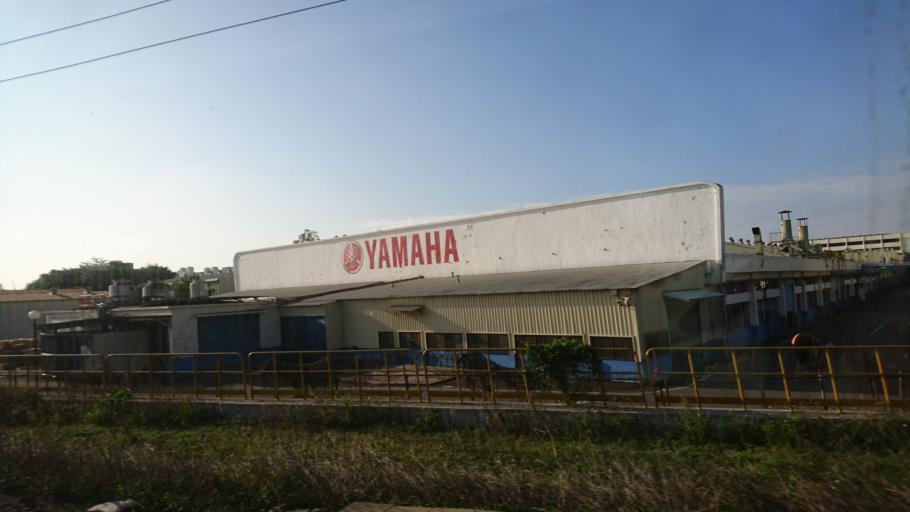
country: TW
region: Taiwan
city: Taoyuan City
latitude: 24.9640
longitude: 121.2455
